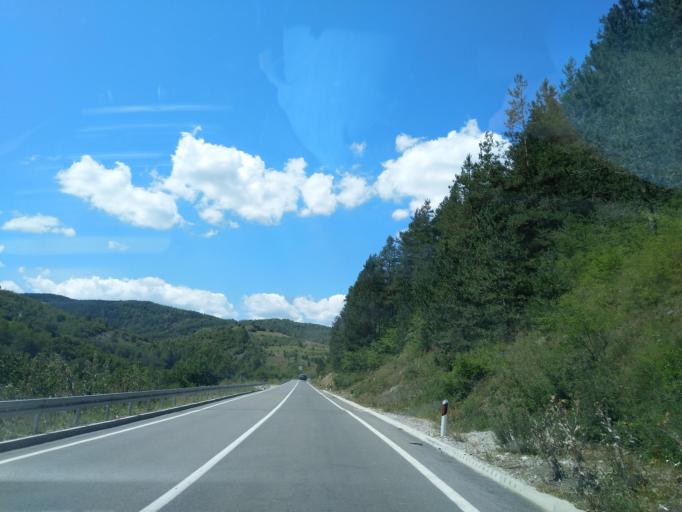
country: RS
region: Central Serbia
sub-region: Zlatiborski Okrug
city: Sjenica
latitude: 43.2826
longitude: 19.9512
